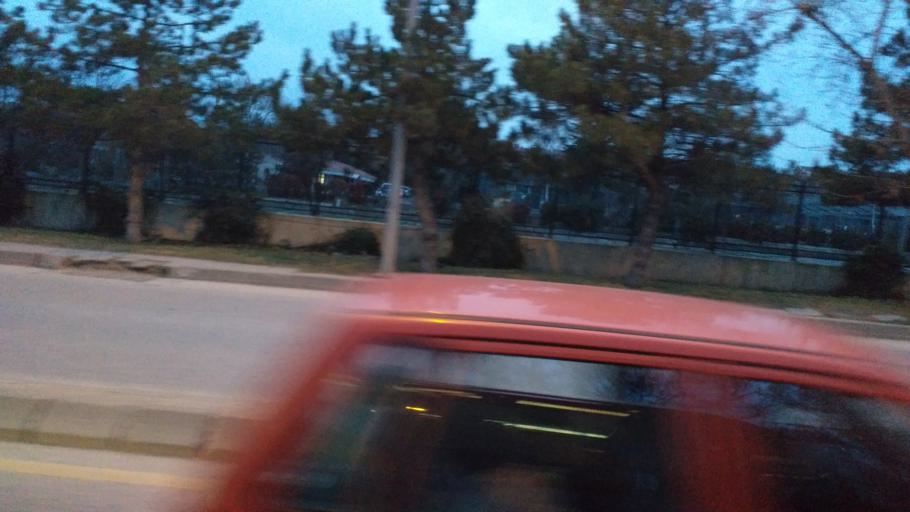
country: TR
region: Ankara
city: Ankara
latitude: 39.9670
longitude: 32.8195
